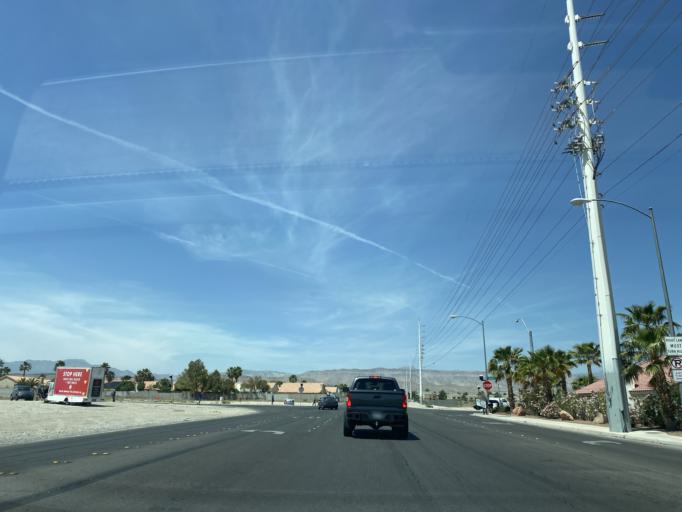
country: US
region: Nevada
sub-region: Clark County
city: Spring Valley
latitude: 36.0850
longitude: -115.2600
